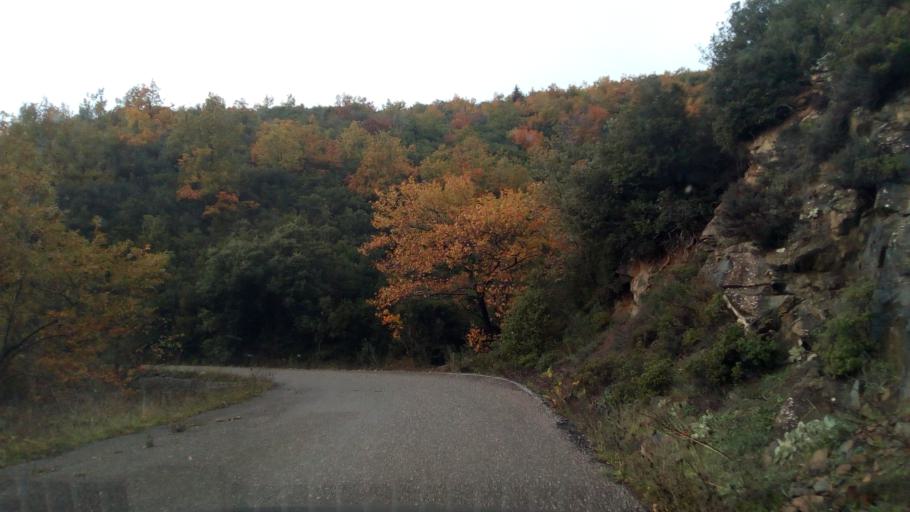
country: GR
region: West Greece
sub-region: Nomos Aitolias kai Akarnanias
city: Nafpaktos
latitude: 38.5212
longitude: 21.9718
